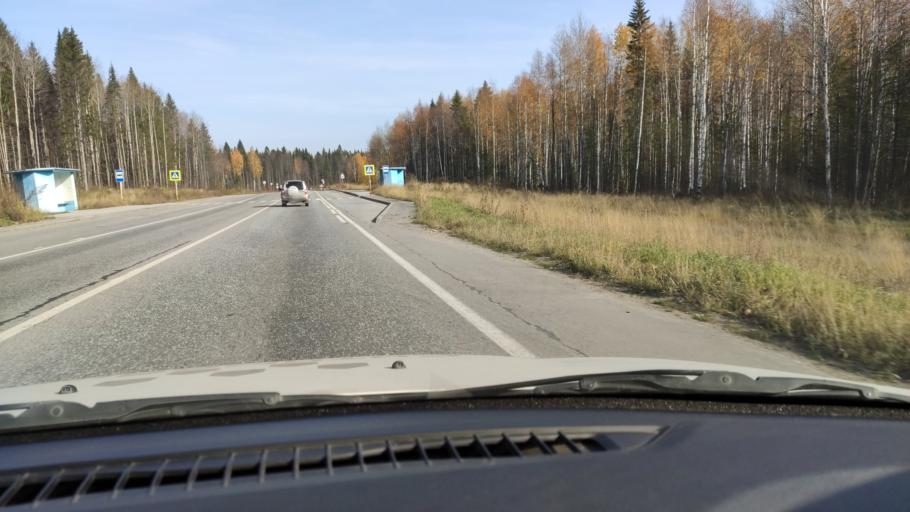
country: RU
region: Perm
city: Novyye Lyady
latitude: 58.0455
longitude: 56.5452
